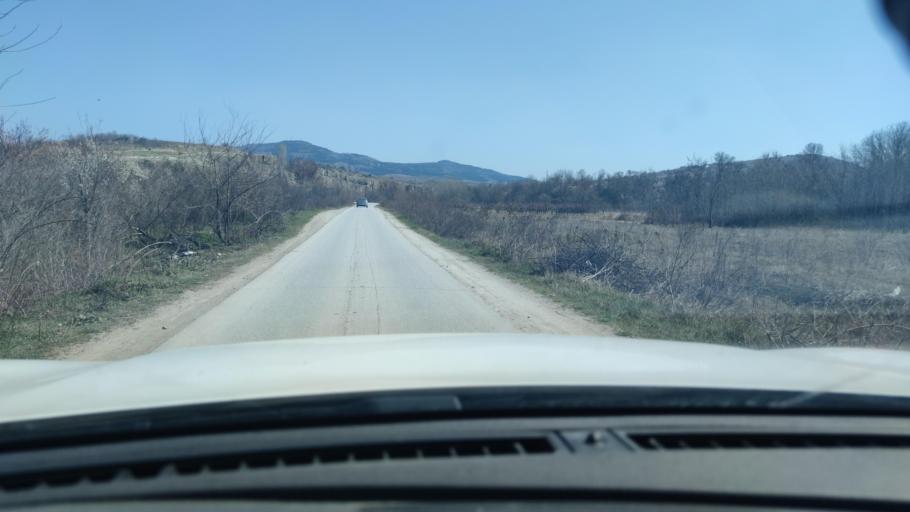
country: MK
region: Rosoman
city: Rosoman
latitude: 41.4728
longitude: 21.9151
